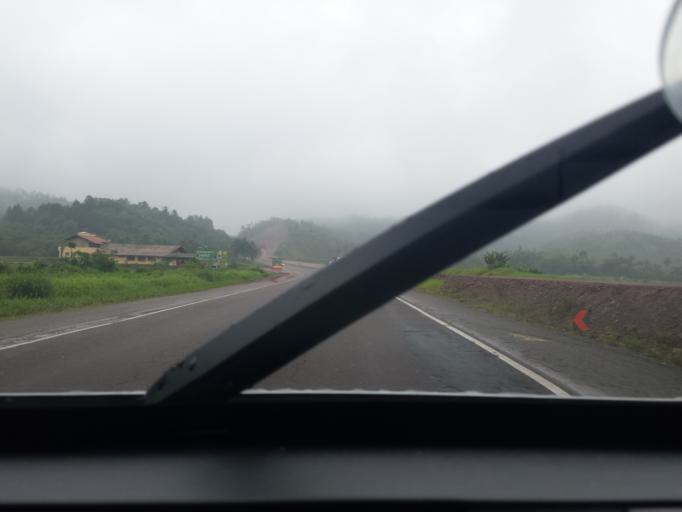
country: BR
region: Santa Catarina
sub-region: Itajai
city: Itajai
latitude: -26.8351
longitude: -48.7568
